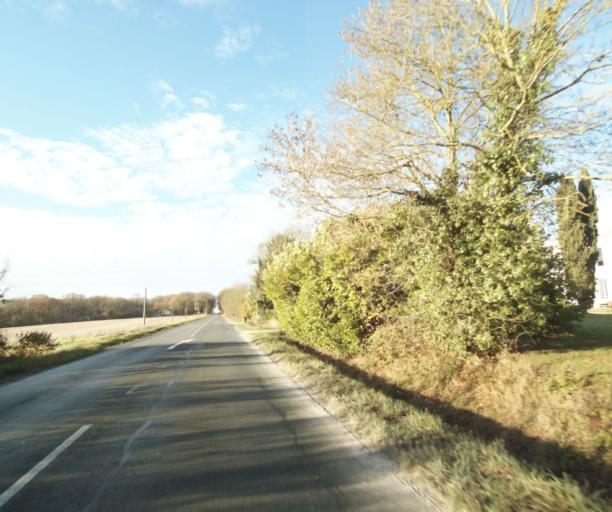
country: FR
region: Poitou-Charentes
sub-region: Departement de la Charente-Maritime
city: Saint-Georges-des-Coteaux
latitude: 45.7366
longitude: -0.7033
